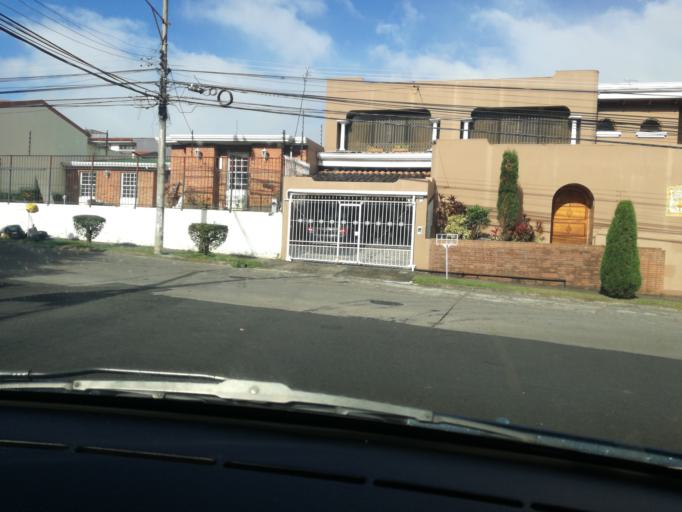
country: CR
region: San Jose
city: San Pedro
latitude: 9.9250
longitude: -84.0427
